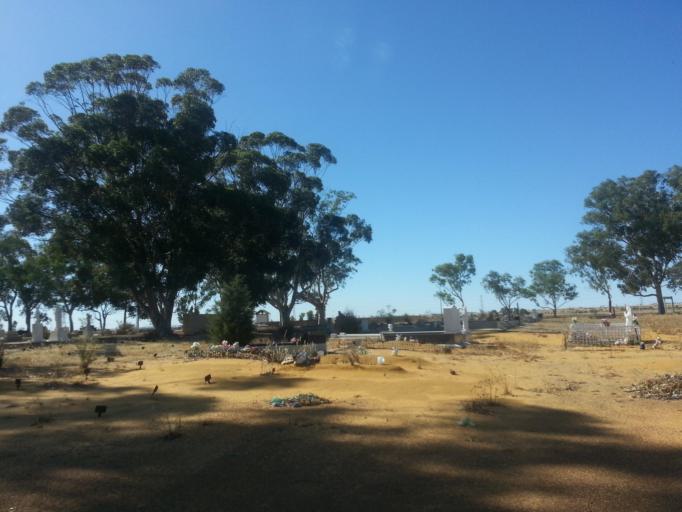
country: AU
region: Western Australia
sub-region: Irwin
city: Dongara
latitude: -29.5153
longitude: 115.7868
